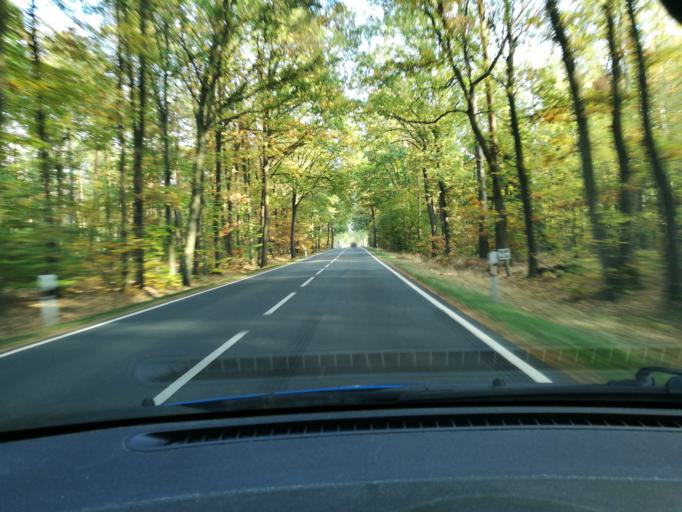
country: DE
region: Lower Saxony
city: Gohrde
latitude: 53.1283
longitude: 10.9088
